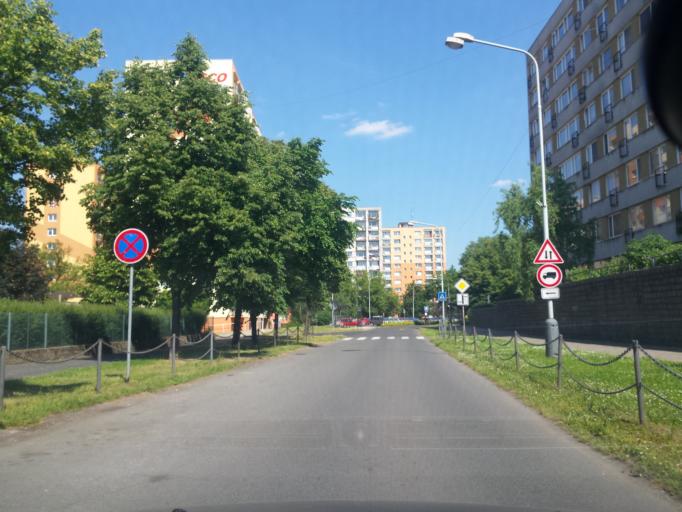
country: CZ
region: Central Bohemia
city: Kralupy nad Vltavou
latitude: 50.2389
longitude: 14.3033
